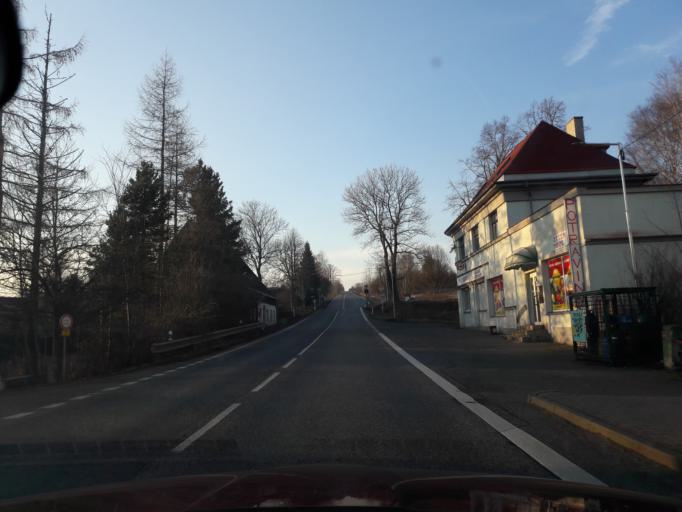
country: CZ
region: Ustecky
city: Dolni Podluzi
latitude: 50.8826
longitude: 14.5794
